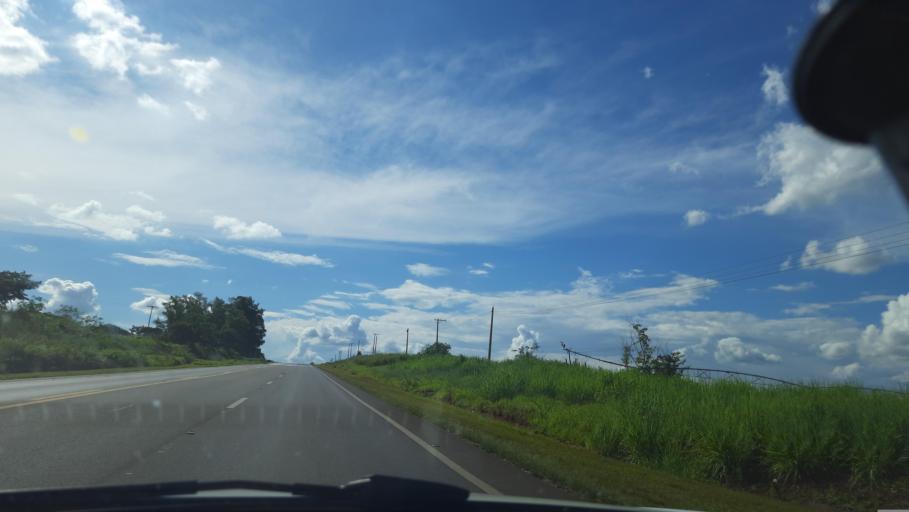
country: BR
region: Sao Paulo
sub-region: Vargem Grande Do Sul
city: Vargem Grande do Sul
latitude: -21.8196
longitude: -46.9677
